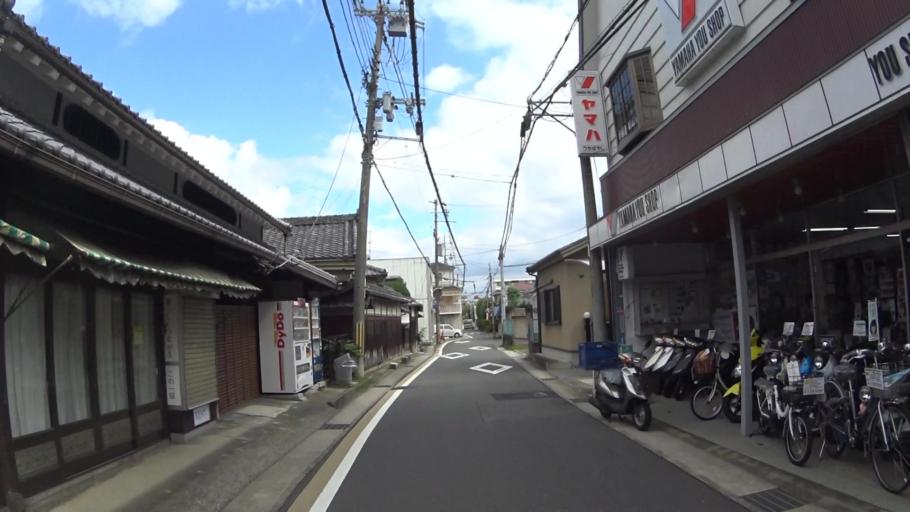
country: JP
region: Kyoto
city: Muko
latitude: 34.9598
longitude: 135.7195
